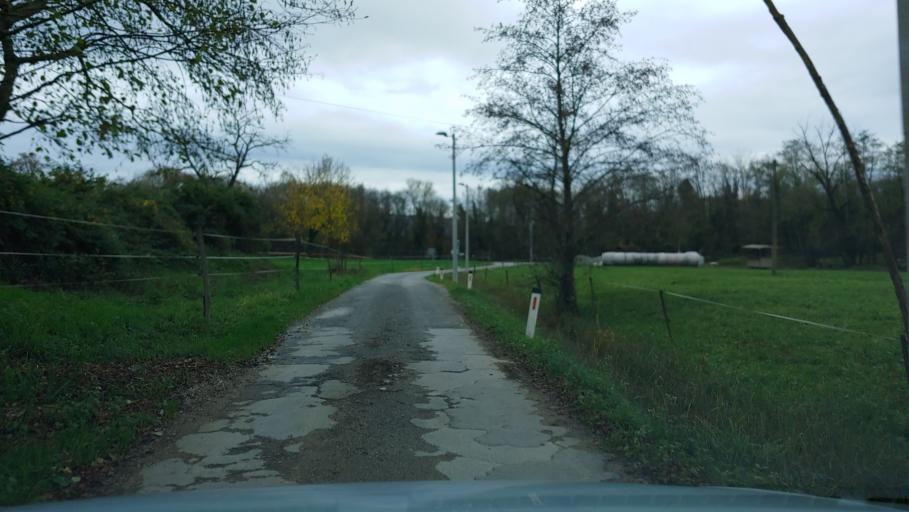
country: SI
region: Sempeter-Vrtojba
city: Sempeter pri Gorici
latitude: 45.9193
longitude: 13.6480
